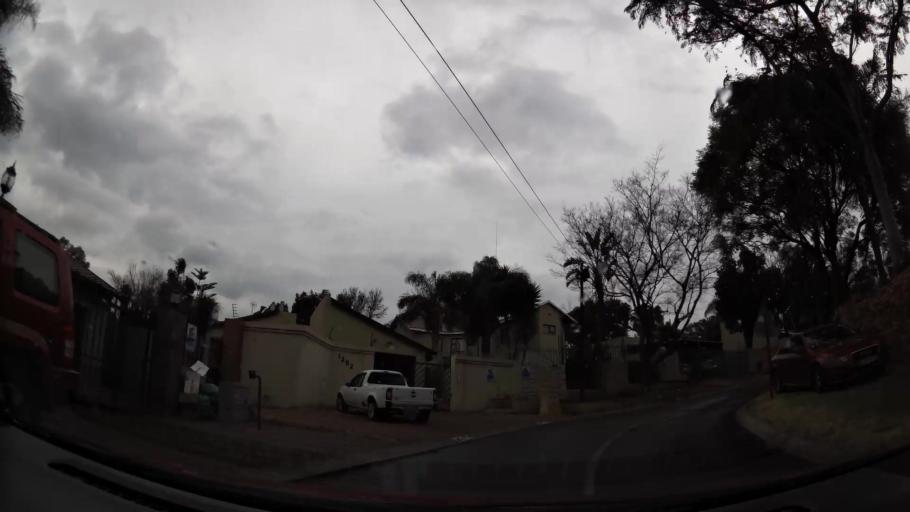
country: ZA
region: Gauteng
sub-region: City of Johannesburg Metropolitan Municipality
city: Roodepoort
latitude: -26.1045
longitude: 27.9211
